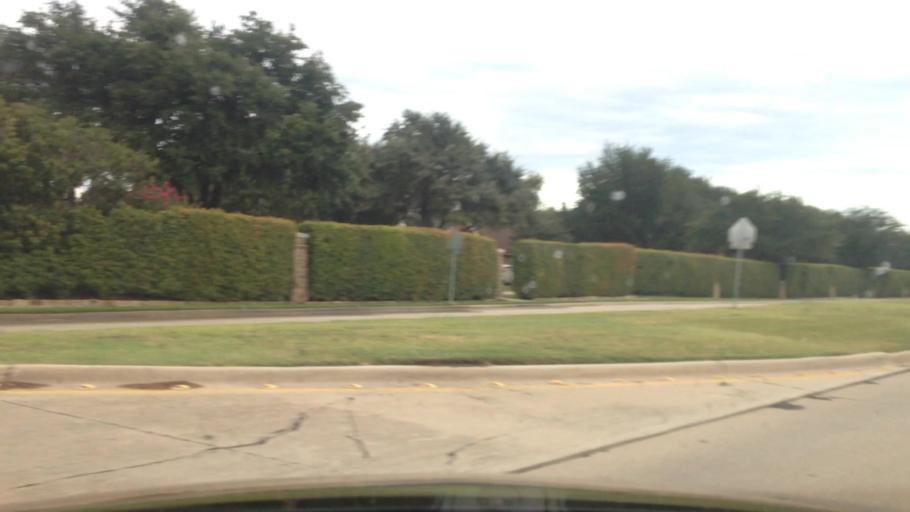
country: US
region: Texas
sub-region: Denton County
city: Flower Mound
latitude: 33.0172
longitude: -97.0522
